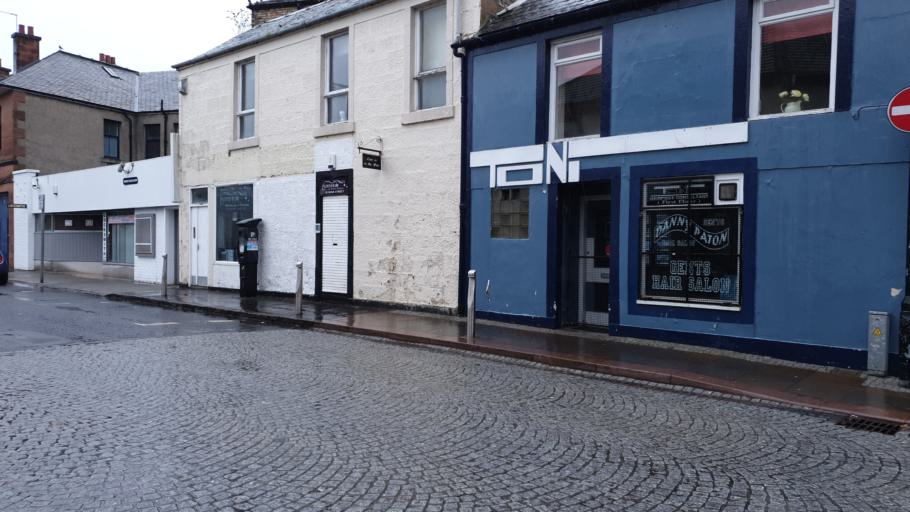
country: GB
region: Scotland
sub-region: East Ayrshire
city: Kilmarnock
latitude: 55.6085
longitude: -4.4990
